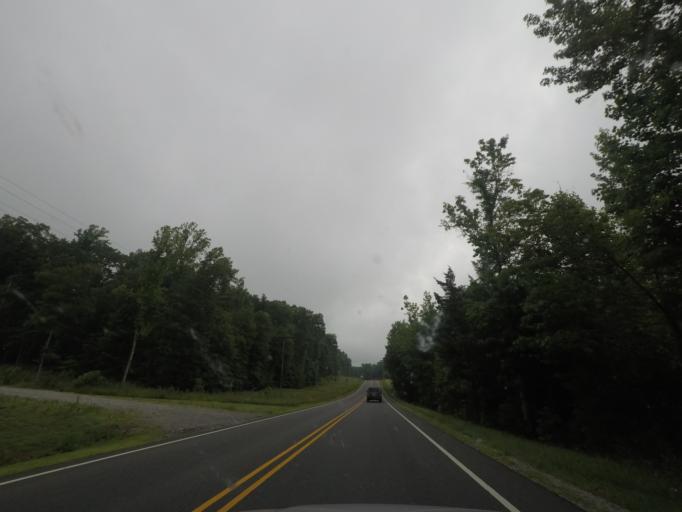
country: US
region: Virginia
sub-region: Prince Edward County
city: Hampden Sydney
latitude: 37.1077
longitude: -78.4681
